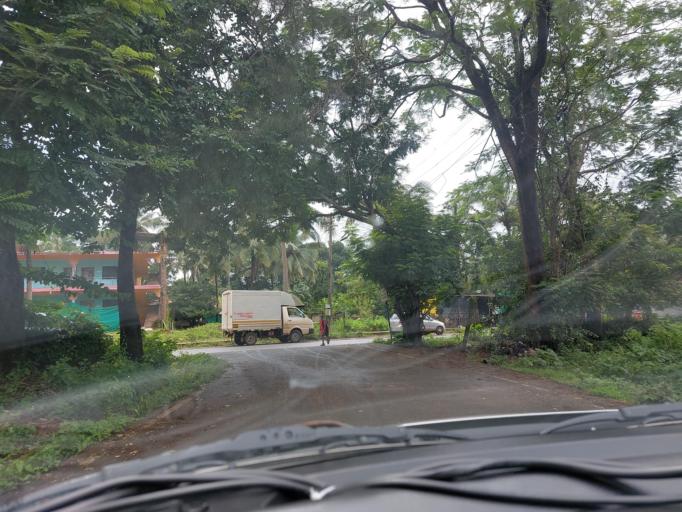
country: IN
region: Goa
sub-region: North Goa
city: Valpoy
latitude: 15.5387
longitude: 74.1377
